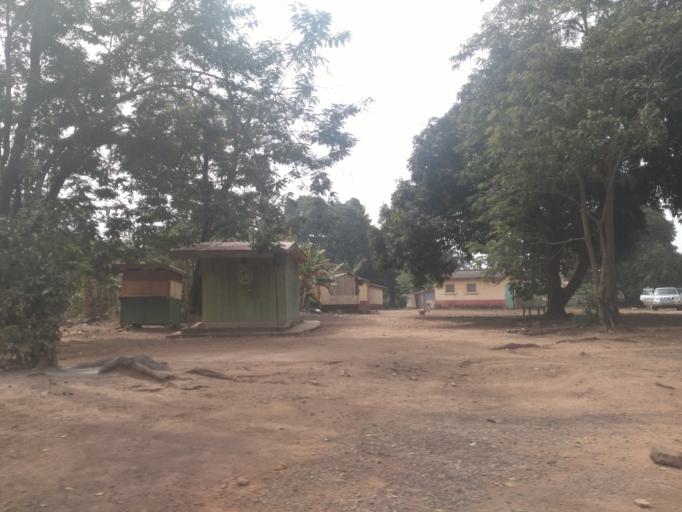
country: GH
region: Ashanti
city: Kumasi
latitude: 6.6876
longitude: -1.6314
